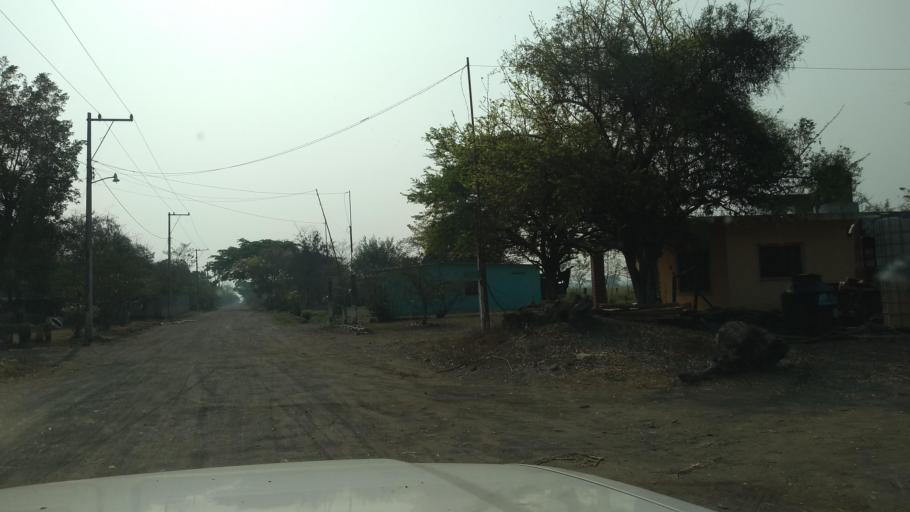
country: MX
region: Oaxaca
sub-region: Cosolapa
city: Cosolapa
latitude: 18.6224
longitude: -96.6059
